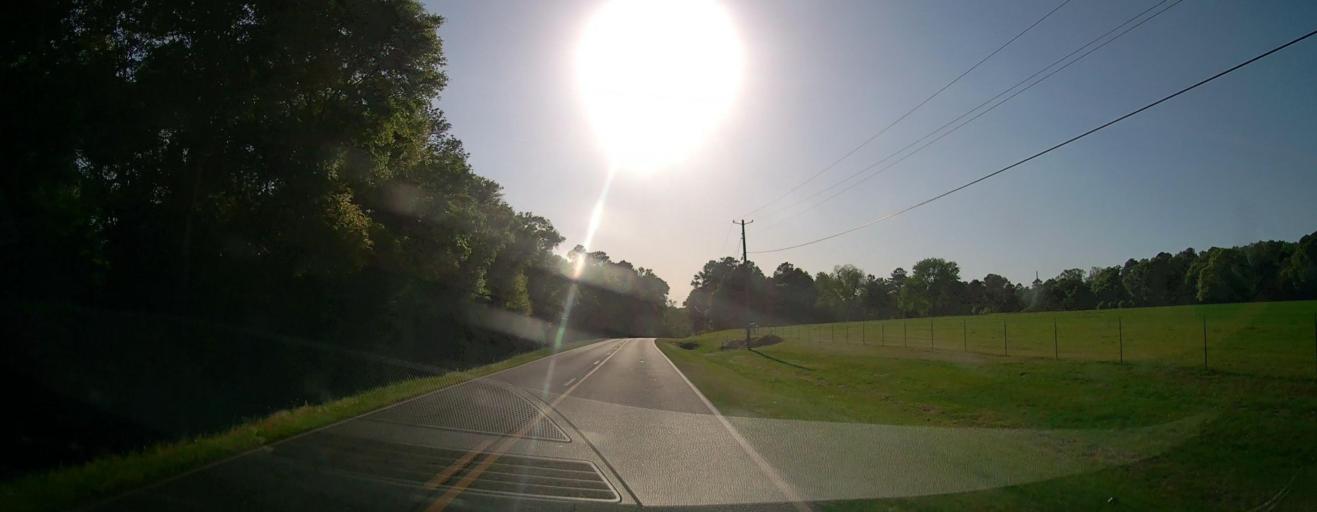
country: US
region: Georgia
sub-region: Macon County
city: Montezuma
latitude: 32.3140
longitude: -84.0024
